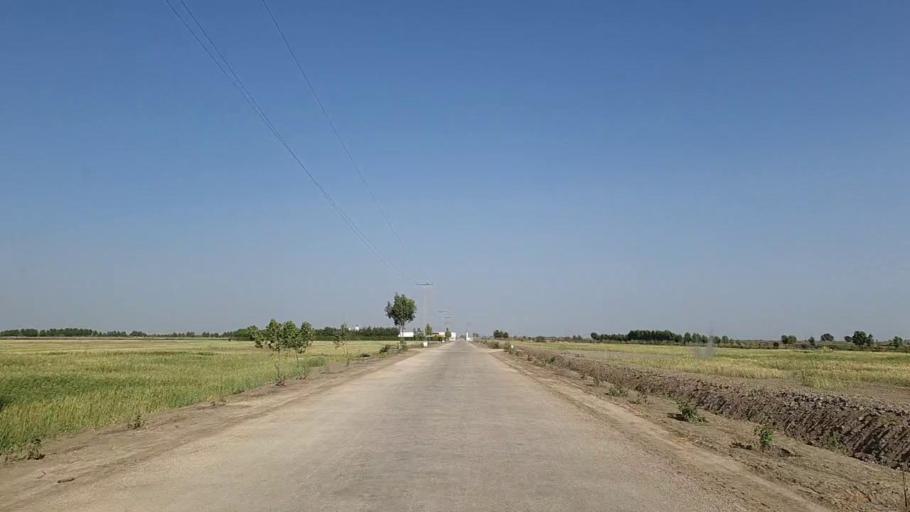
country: PK
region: Sindh
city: Jati
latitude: 24.5142
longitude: 68.1825
